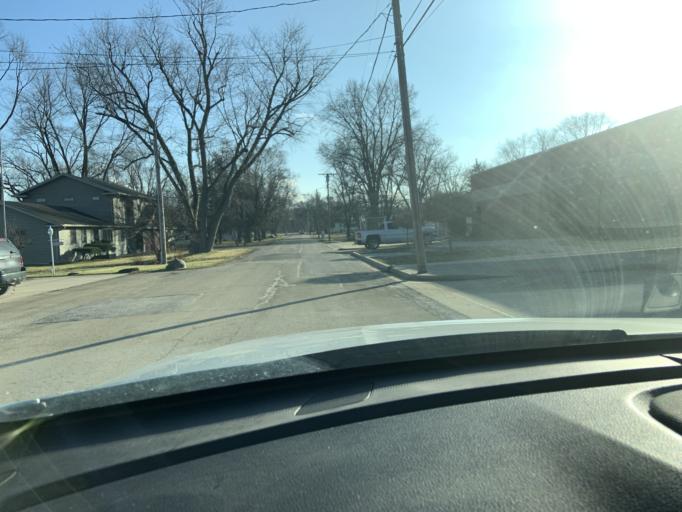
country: US
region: Illinois
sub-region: LaSalle County
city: Seneca
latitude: 41.3091
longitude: -88.6064
